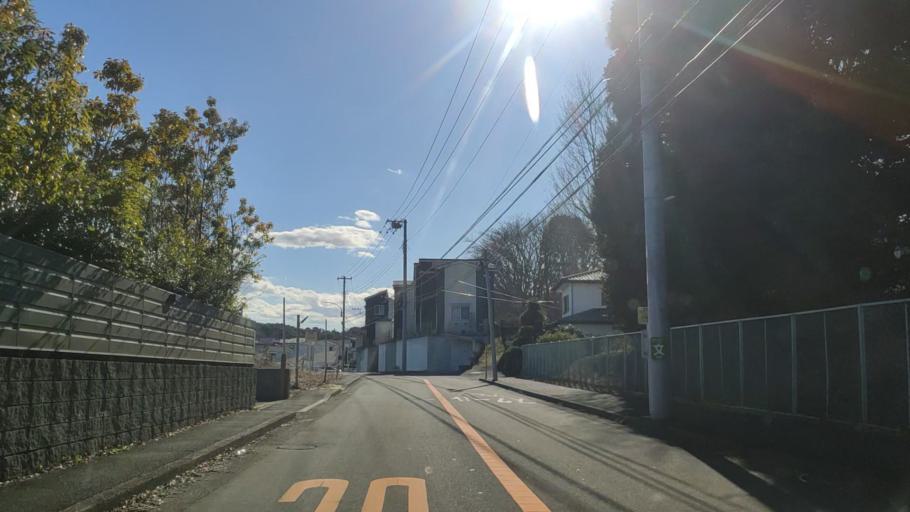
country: JP
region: Kanagawa
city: Minami-rinkan
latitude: 35.5104
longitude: 139.5264
